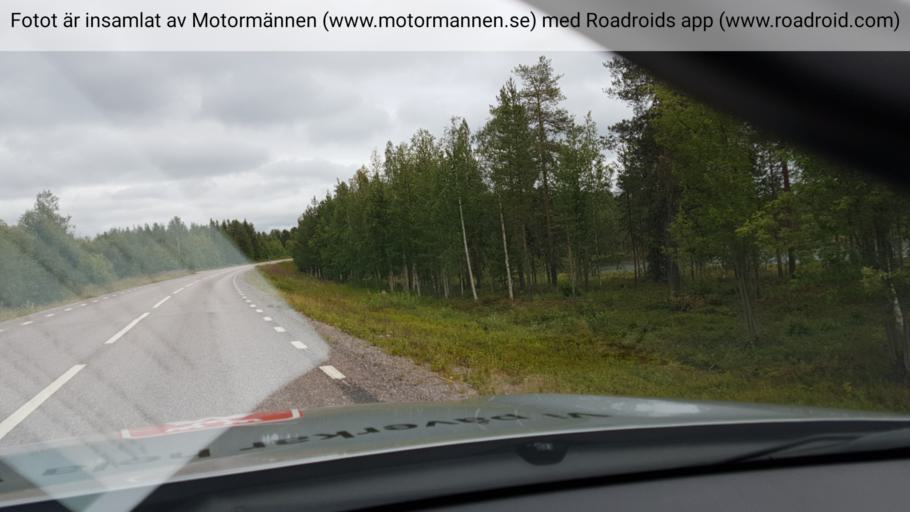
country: SE
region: Norrbotten
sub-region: Gallivare Kommun
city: Gaellivare
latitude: 67.0627
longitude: 21.2686
